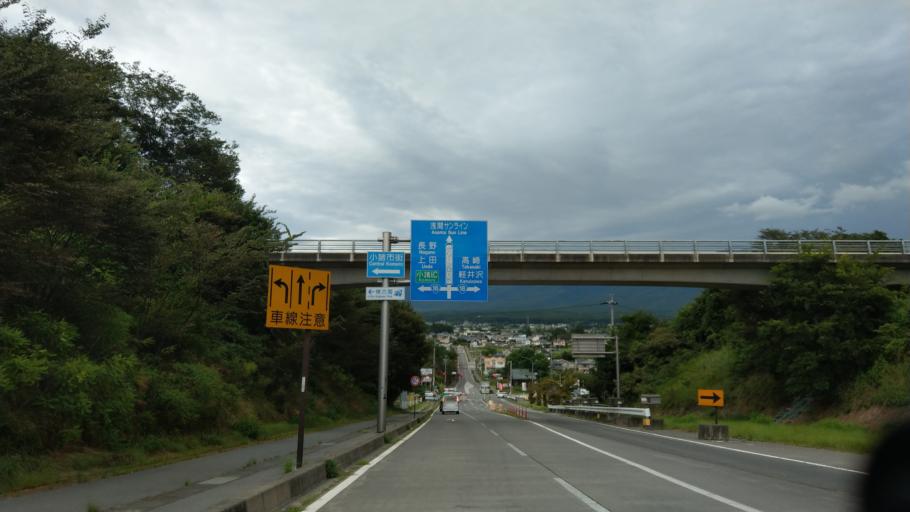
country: JP
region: Nagano
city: Komoro
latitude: 36.3115
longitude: 138.4567
